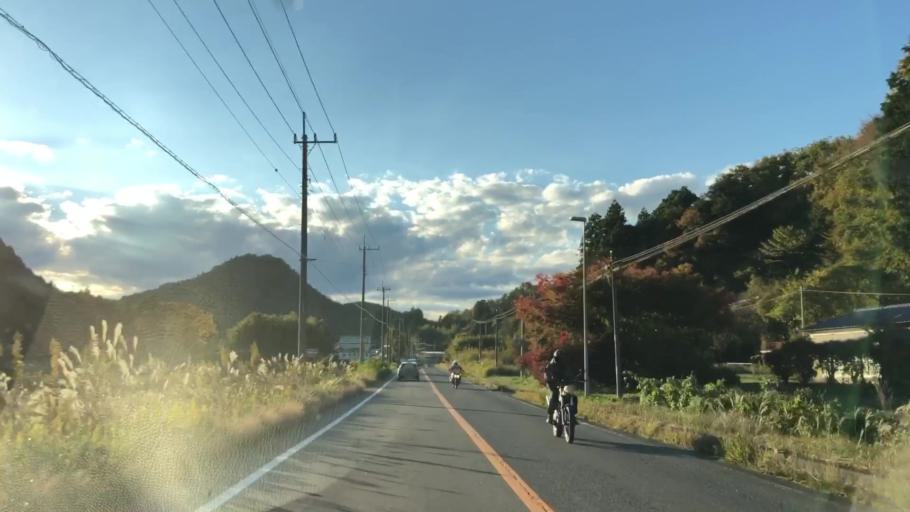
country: JP
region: Tochigi
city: Motegi
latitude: 36.4944
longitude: 140.2629
